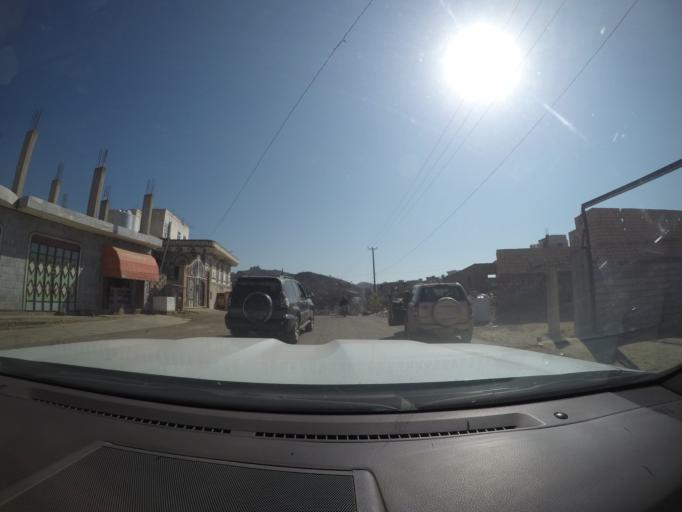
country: YE
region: Ad Dali'
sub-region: Ad Dhale'e
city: Dhalie
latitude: 13.6975
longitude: 44.7349
